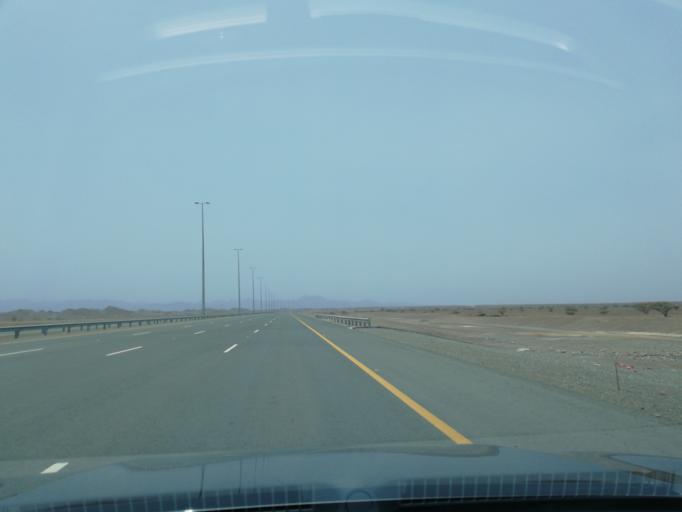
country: OM
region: Al Batinah
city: Al Liwa'
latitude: 24.5515
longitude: 56.4799
